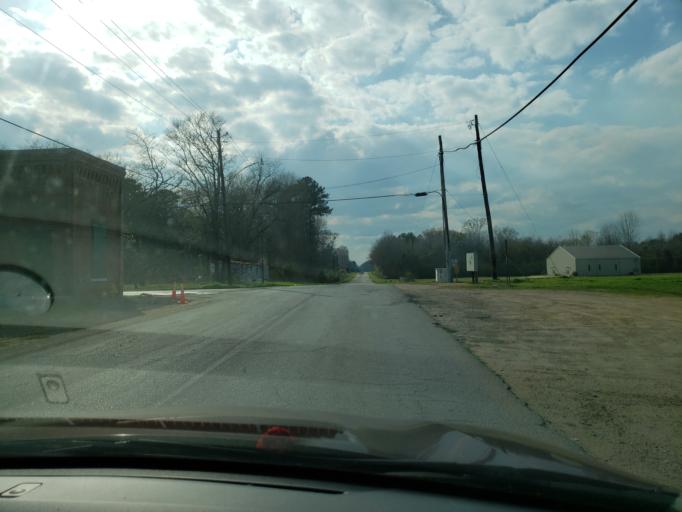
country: US
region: Alabama
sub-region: Hale County
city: Greensboro
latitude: 32.6997
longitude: -87.6090
